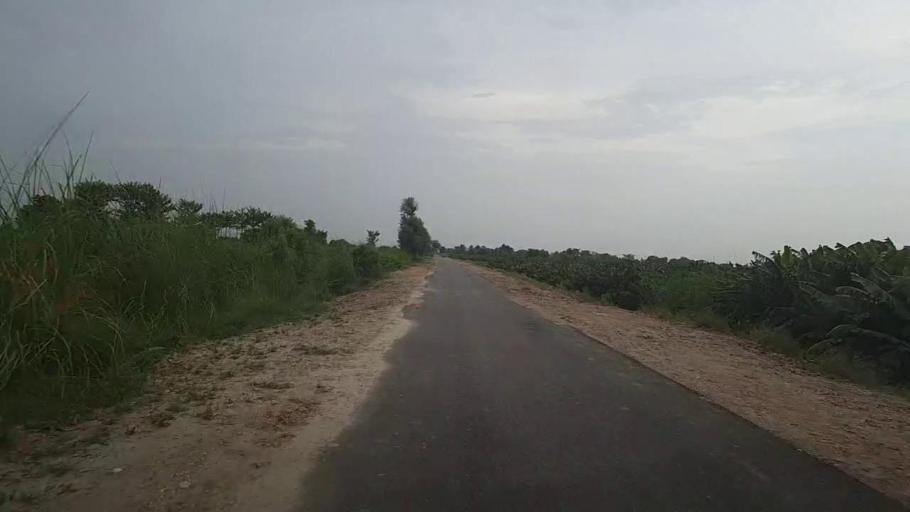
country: PK
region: Sindh
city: Karaundi
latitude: 26.9733
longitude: 68.3606
